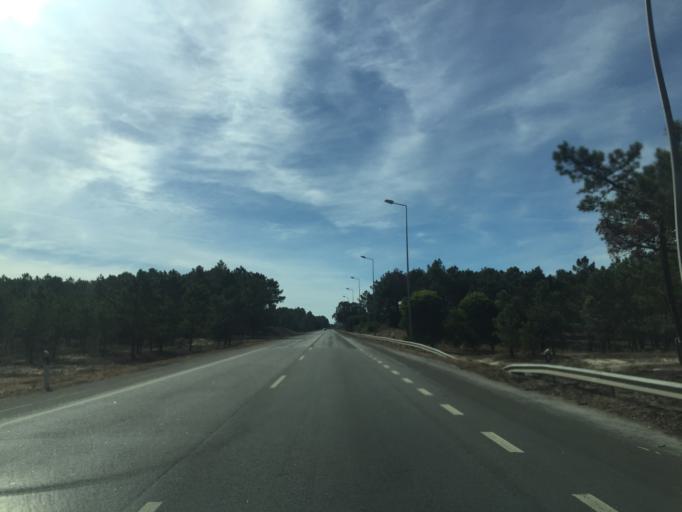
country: PT
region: Coimbra
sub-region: Figueira da Foz
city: Lavos
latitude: 40.0994
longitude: -8.8549
